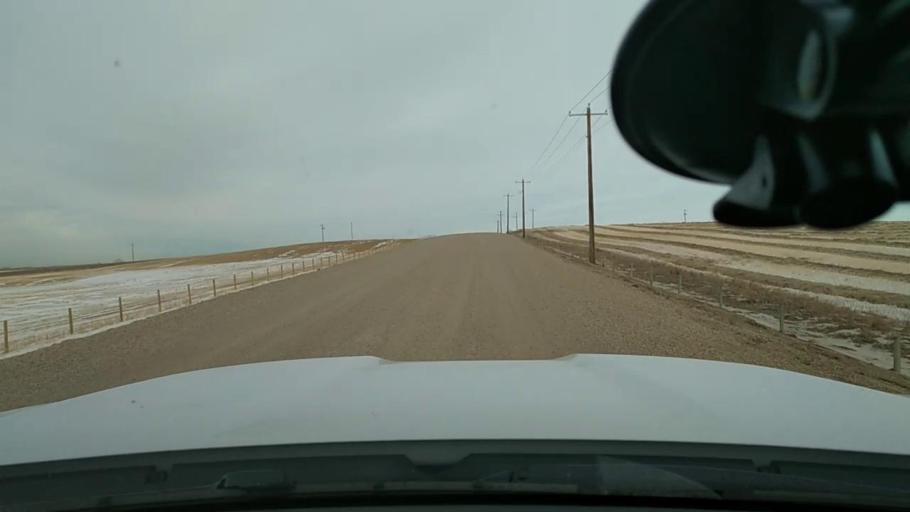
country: CA
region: Alberta
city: Airdrie
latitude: 51.2387
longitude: -113.9118
